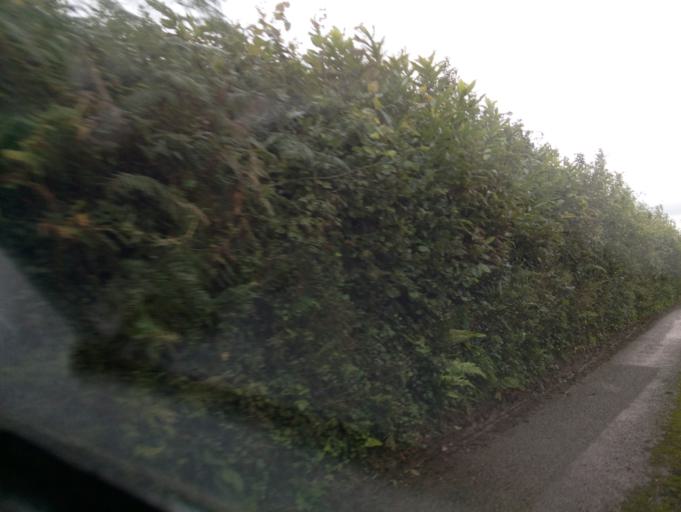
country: GB
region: England
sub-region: Devon
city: Totnes
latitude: 50.3298
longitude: -3.6841
